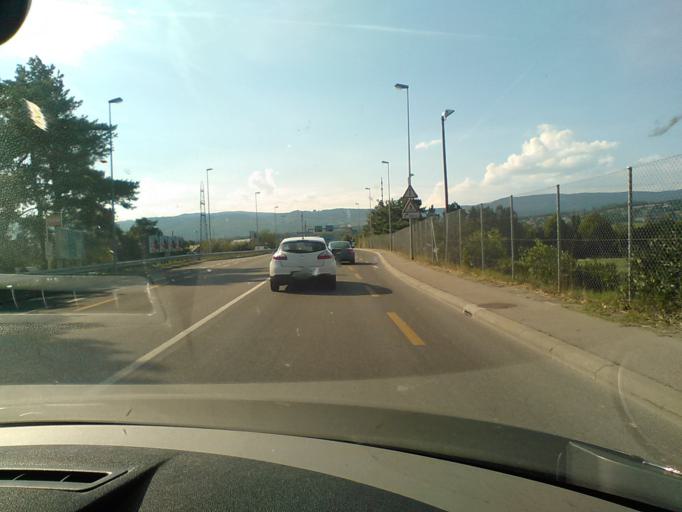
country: CH
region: Vaud
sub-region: Nyon District
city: Gland
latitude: 46.4236
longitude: 6.2596
